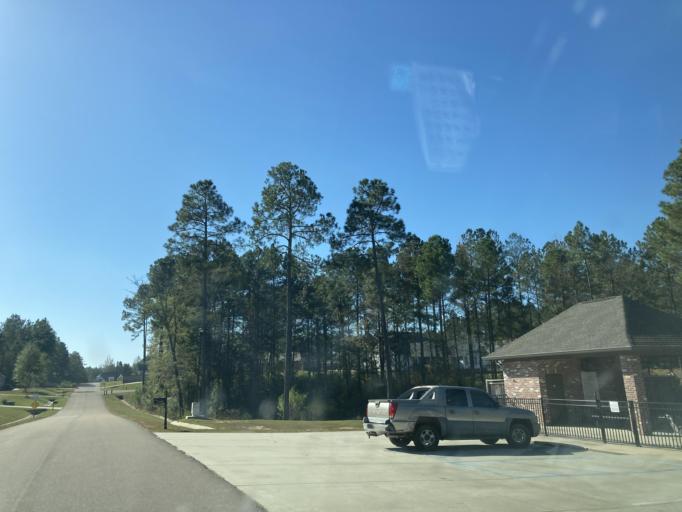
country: US
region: Mississippi
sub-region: Lamar County
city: Sumrall
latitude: 31.3332
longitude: -89.4848
